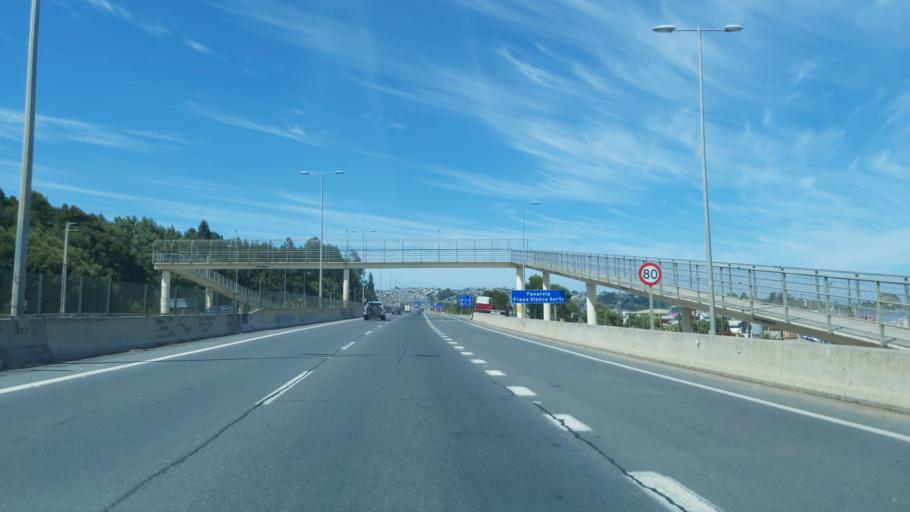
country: CL
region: Biobio
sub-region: Provincia de Concepcion
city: Coronel
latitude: -37.0627
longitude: -73.1414
